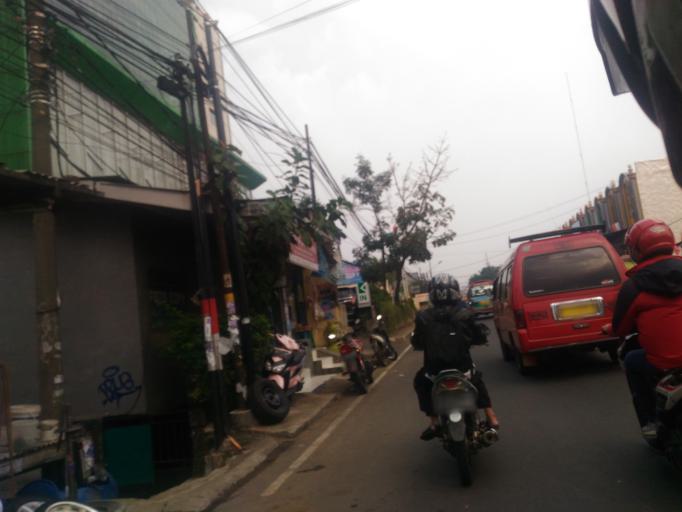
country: ID
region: West Java
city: Bogor
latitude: -6.6381
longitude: 106.8316
